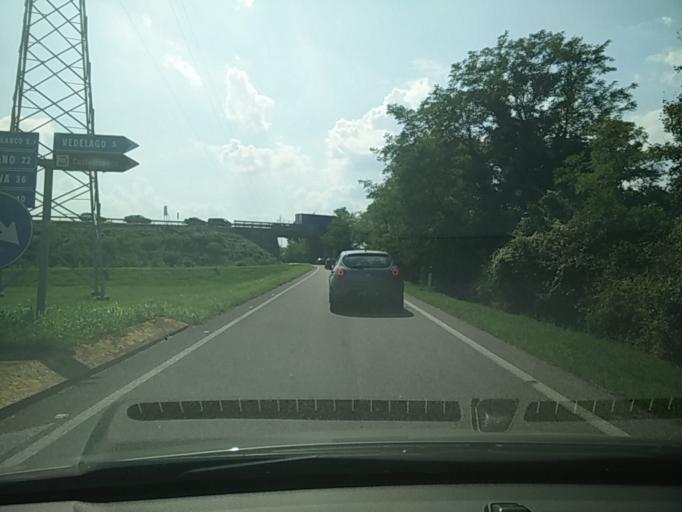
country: IT
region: Veneto
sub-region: Provincia di Treviso
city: Salvatronda
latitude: 45.6858
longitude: 11.9684
